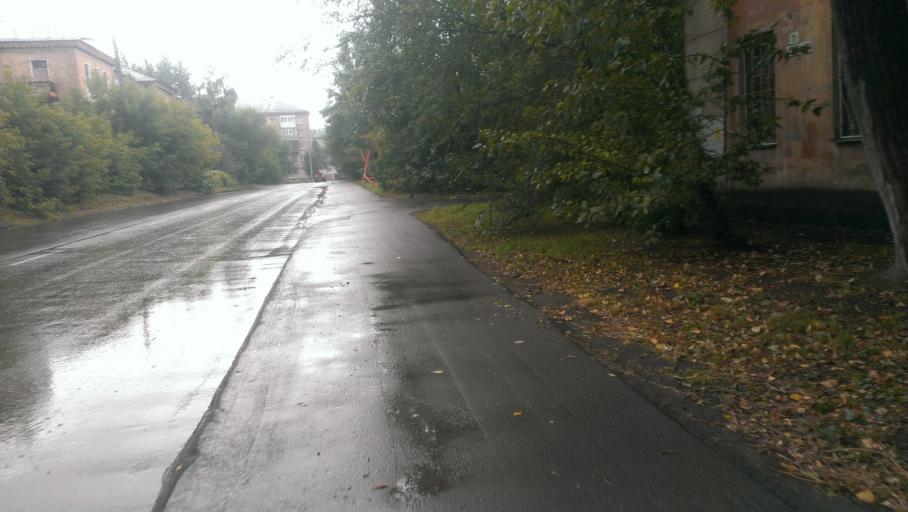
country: RU
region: Altai Krai
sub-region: Gorod Barnaulskiy
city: Barnaul
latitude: 53.3583
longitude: 83.7636
